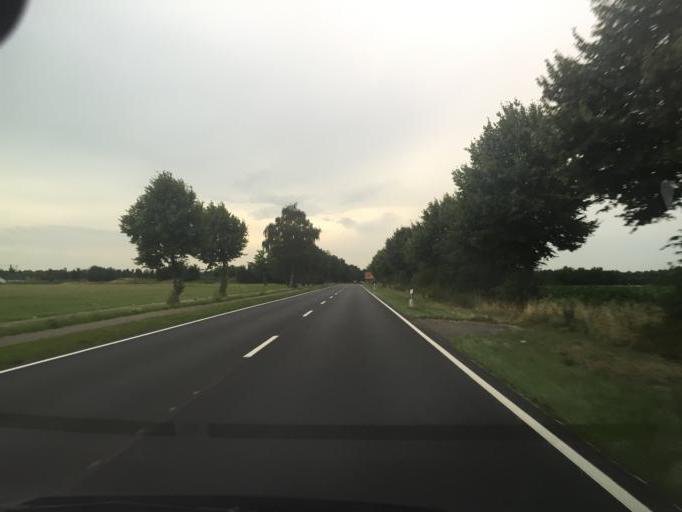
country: DE
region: North Rhine-Westphalia
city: Erkelenz
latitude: 51.0974
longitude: 6.3222
